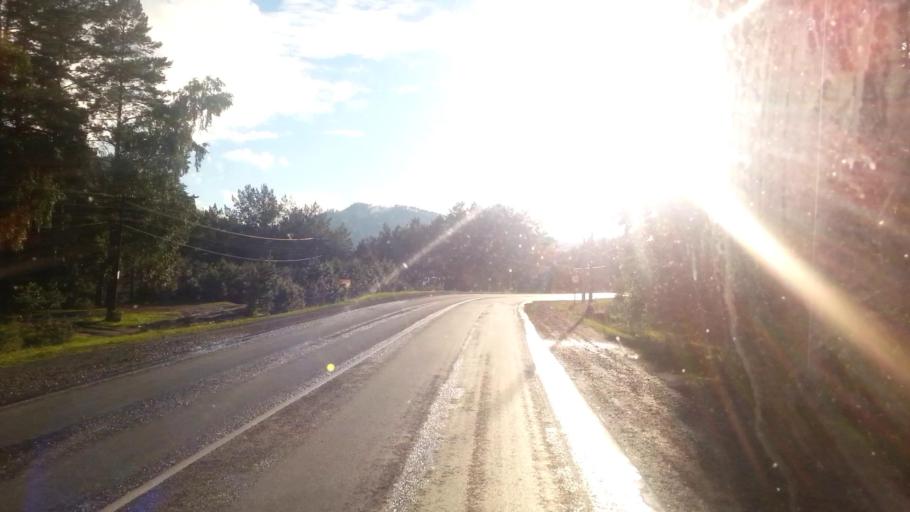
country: RU
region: Altay
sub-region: Mayminskiy Rayon
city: Manzherok
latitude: 51.8311
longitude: 85.7622
